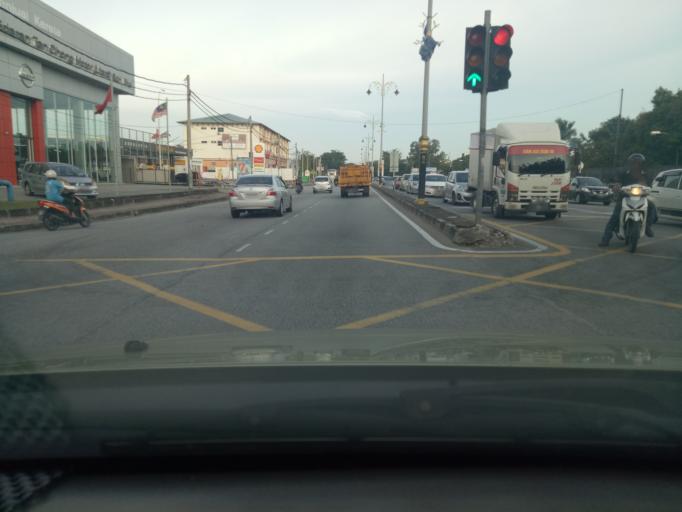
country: MY
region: Kedah
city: Alor Setar
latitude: 6.1273
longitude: 100.3526
